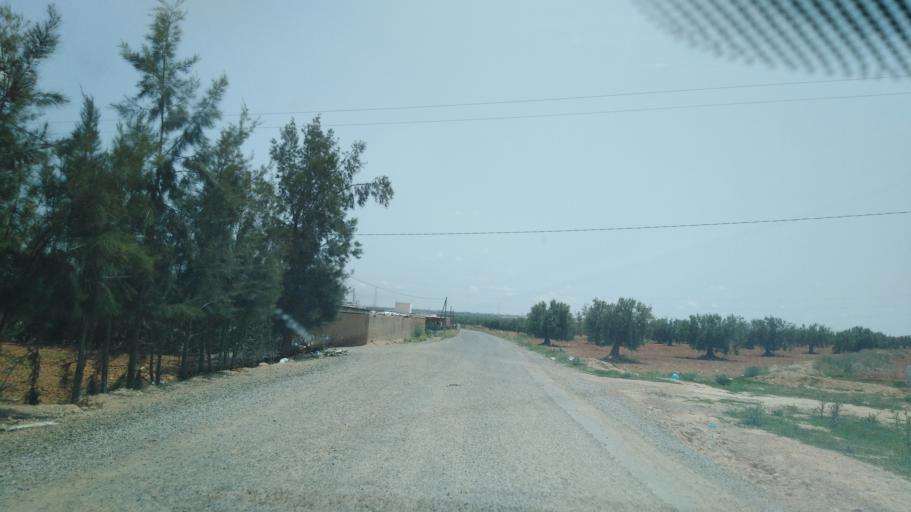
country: TN
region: Safaqis
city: Sfax
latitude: 34.7490
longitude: 10.5700
